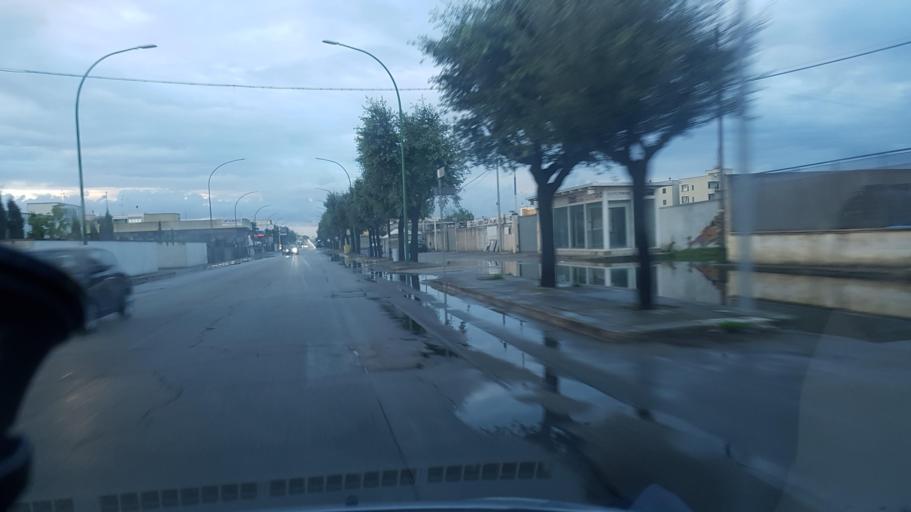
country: IT
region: Apulia
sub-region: Provincia di Lecce
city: Surbo
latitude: 40.3841
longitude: 18.1354
